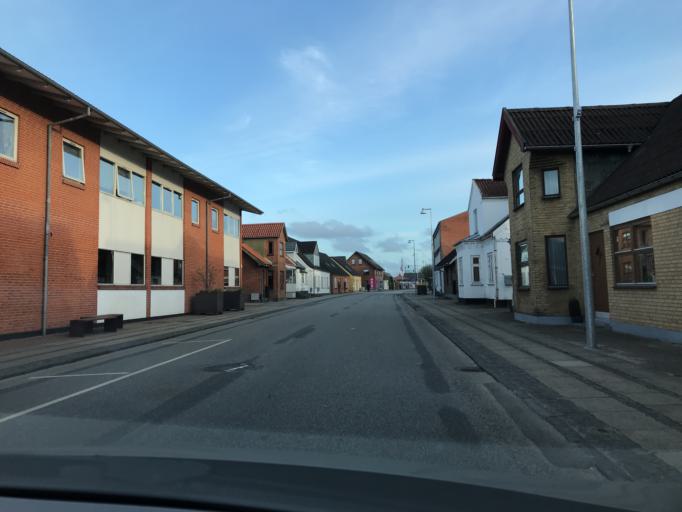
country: DK
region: Central Jutland
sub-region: Herning Kommune
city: Sunds
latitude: 56.2044
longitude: 9.0161
